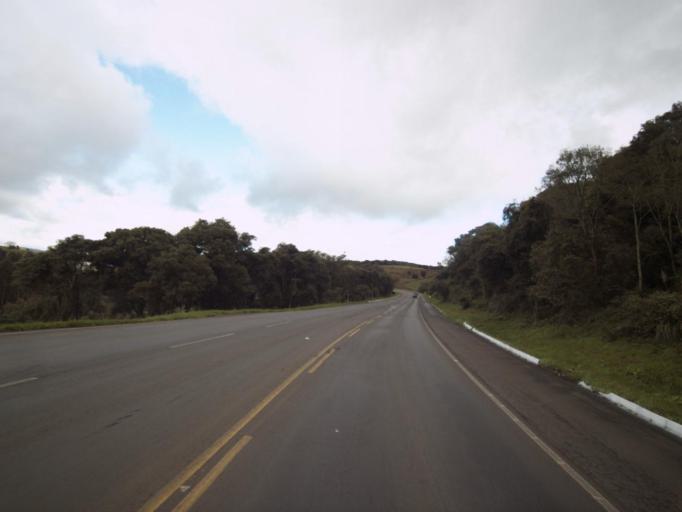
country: BR
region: Santa Catarina
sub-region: Concordia
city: Concordia
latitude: -27.0840
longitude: -51.9075
